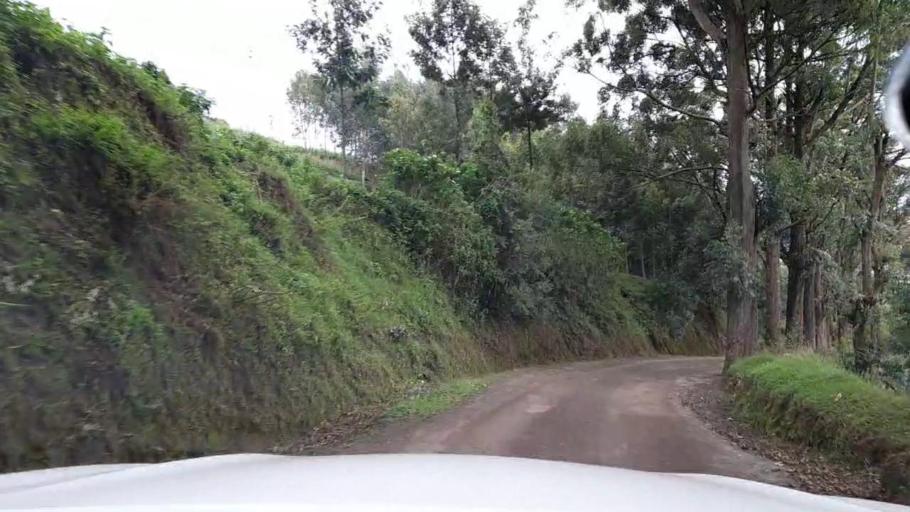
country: BI
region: Kayanza
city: Kayanza
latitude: -2.7943
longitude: 29.5107
